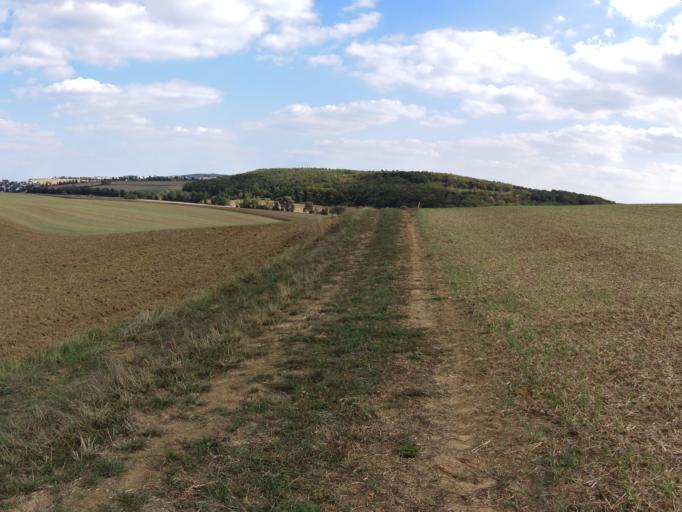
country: DE
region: Bavaria
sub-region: Regierungsbezirk Unterfranken
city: Hettstadt
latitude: 49.7945
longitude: 9.8001
